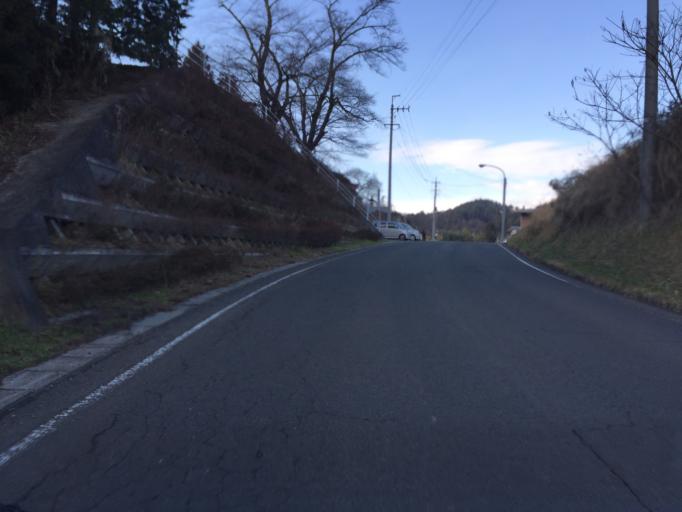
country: JP
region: Fukushima
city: Fukushima-shi
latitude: 37.7169
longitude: 140.4262
